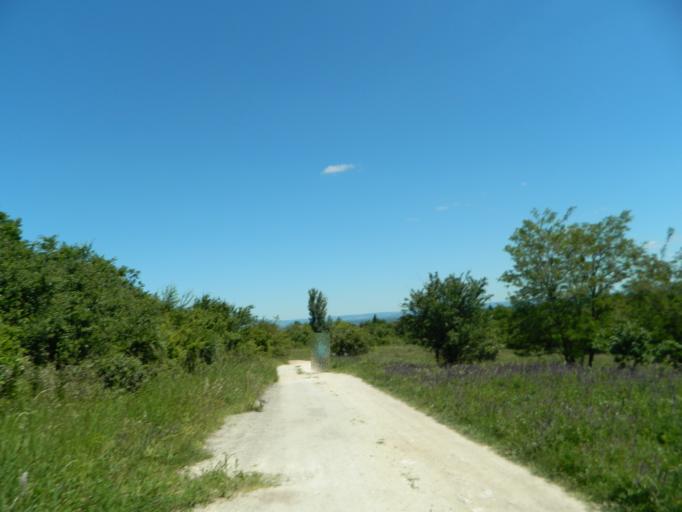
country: HU
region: Pest
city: Budakalasz
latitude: 47.6071
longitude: 19.0345
